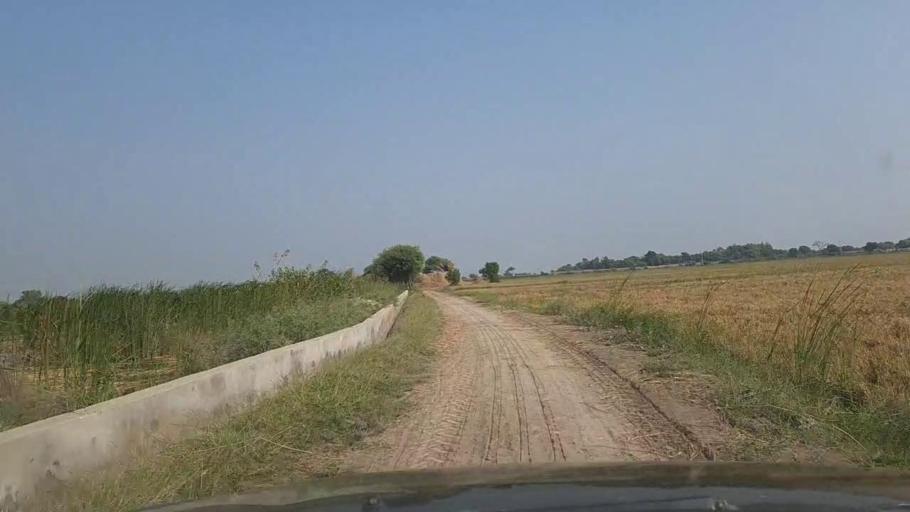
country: PK
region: Sindh
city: Mirpur Batoro
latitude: 24.6965
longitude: 68.2527
